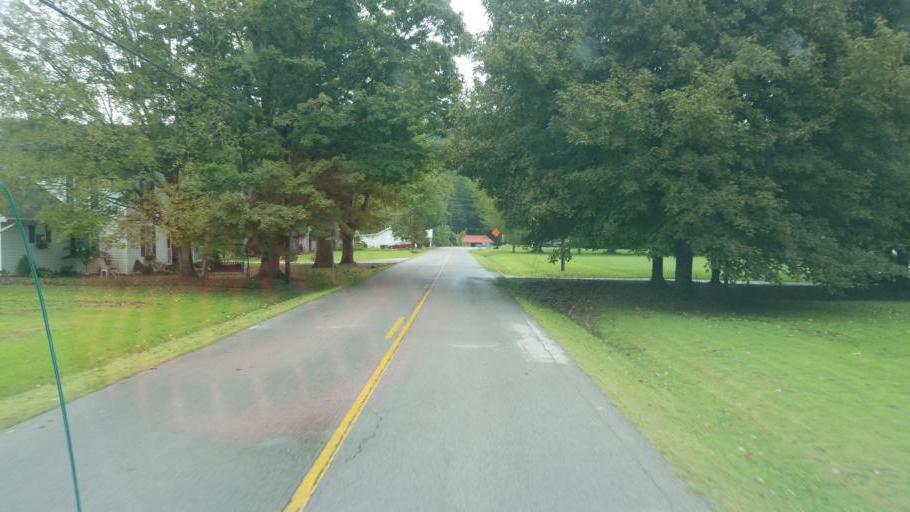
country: US
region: Kentucky
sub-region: Rowan County
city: Morehead
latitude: 38.3518
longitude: -83.5284
